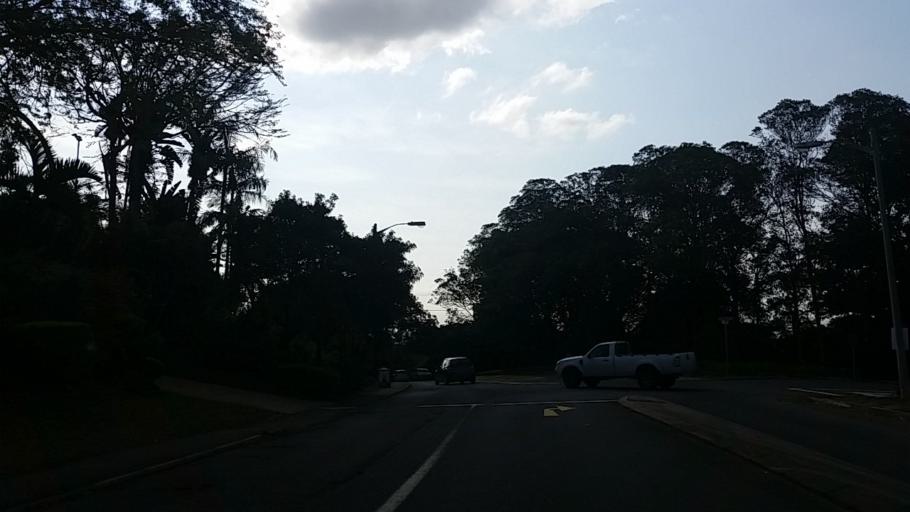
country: ZA
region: KwaZulu-Natal
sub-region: eThekwini Metropolitan Municipality
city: Berea
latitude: -29.8322
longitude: 30.9216
